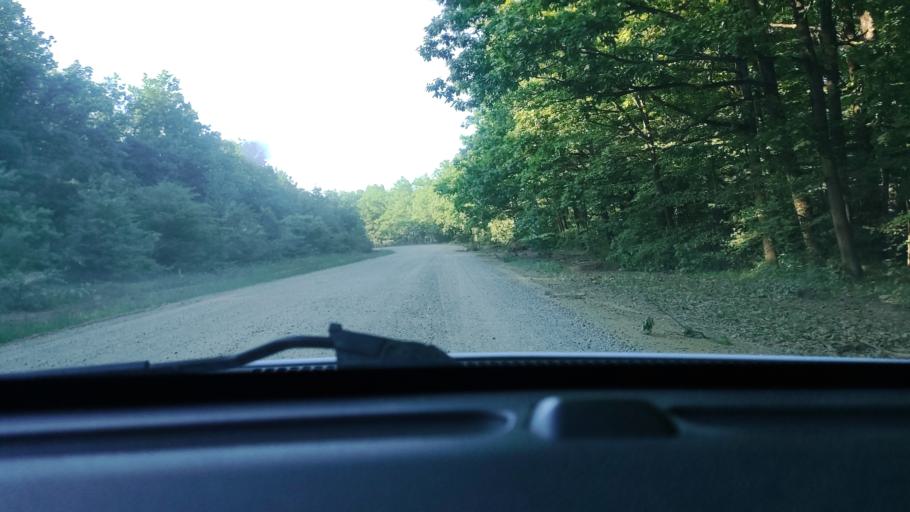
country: RU
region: Krasnodarskiy
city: Novodmitriyevskaya
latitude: 44.7167
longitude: 38.9915
